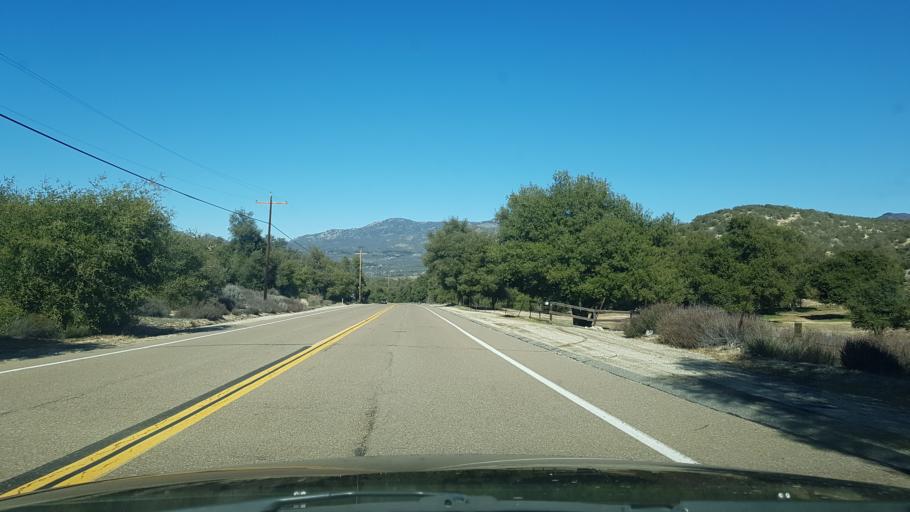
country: US
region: California
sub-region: San Diego County
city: Julian
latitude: 33.2077
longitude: -116.6036
